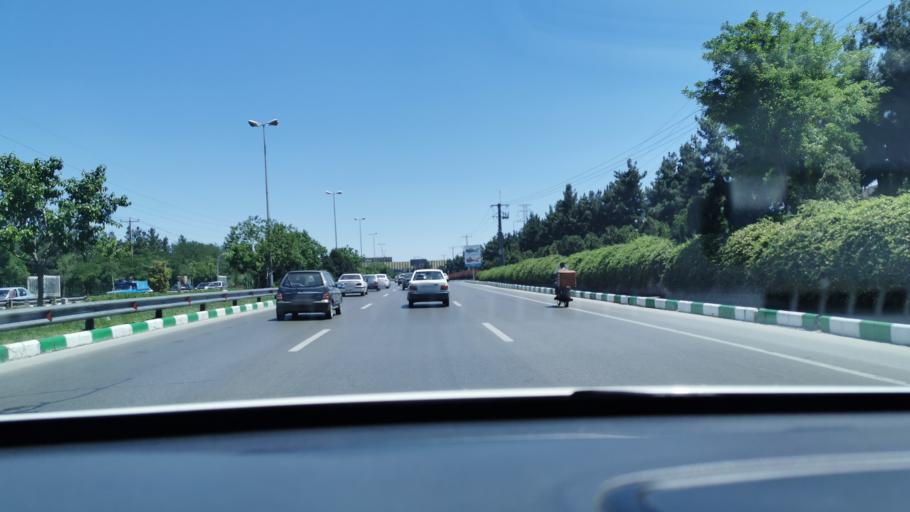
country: IR
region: Razavi Khorasan
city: Mashhad
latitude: 36.2604
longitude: 59.5856
